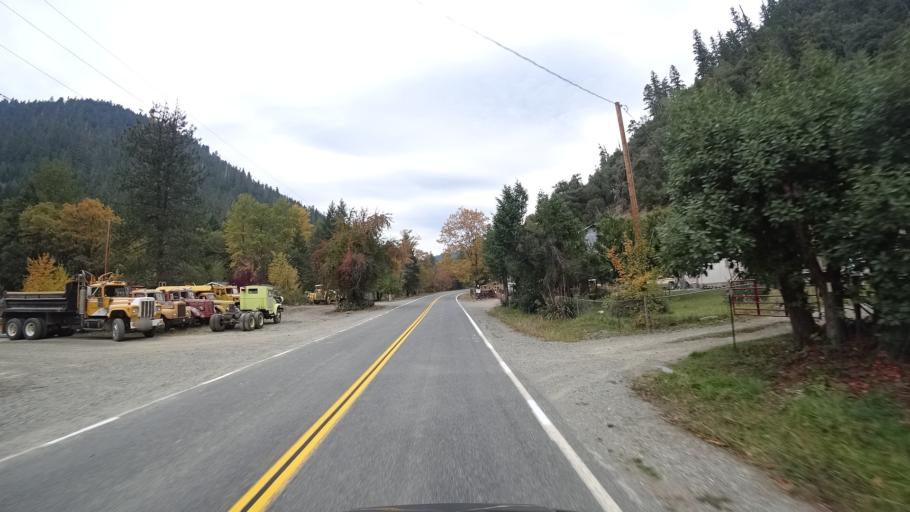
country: US
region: California
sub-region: Siskiyou County
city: Happy Camp
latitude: 41.8871
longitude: -123.4327
